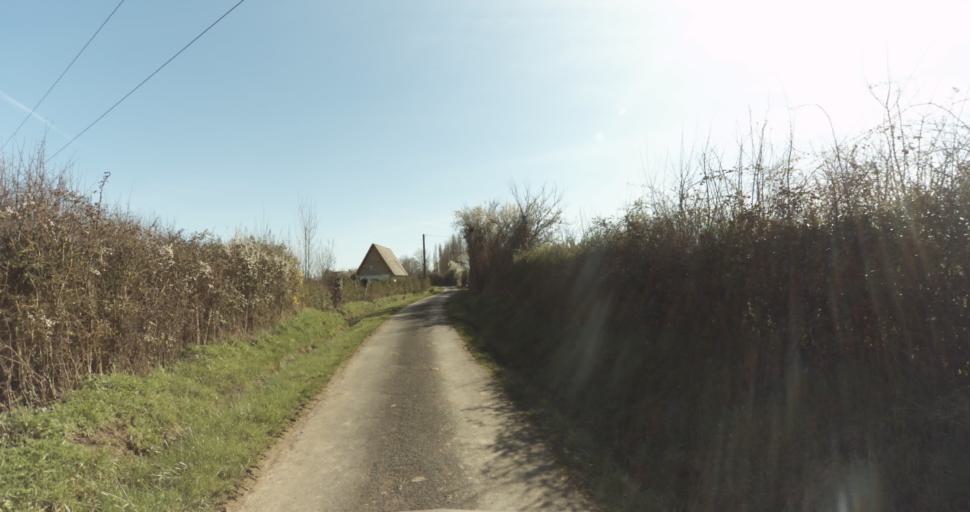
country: FR
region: Lower Normandy
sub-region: Departement du Calvados
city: Saint-Pierre-sur-Dives
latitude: 49.0305
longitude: 0.0198
